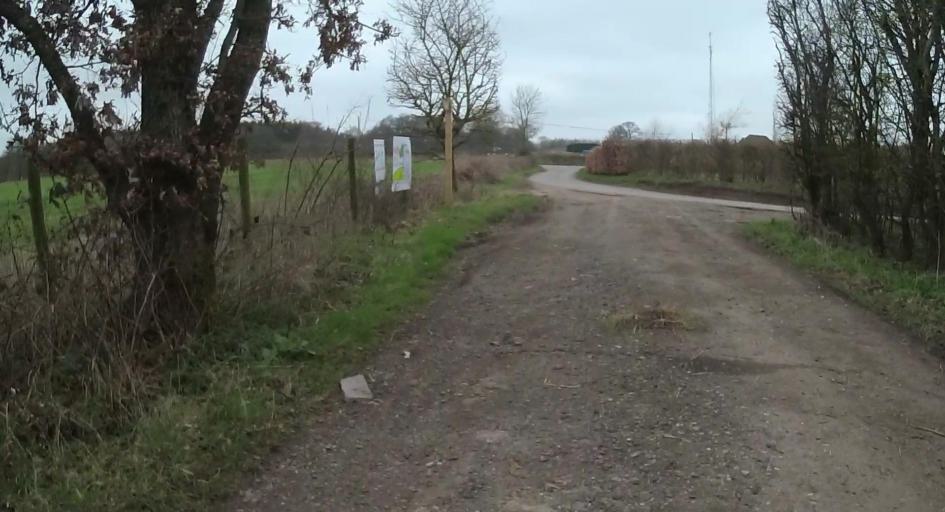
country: GB
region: England
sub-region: Hampshire
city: Four Marks
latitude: 51.1353
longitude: -1.1059
